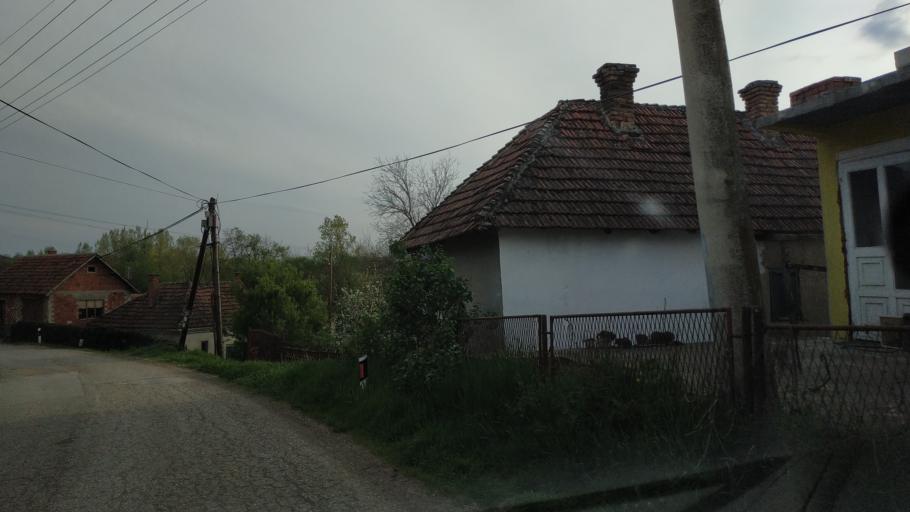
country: RS
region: Central Serbia
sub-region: Nisavski Okrug
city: Aleksinac
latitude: 43.4880
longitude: 21.8181
